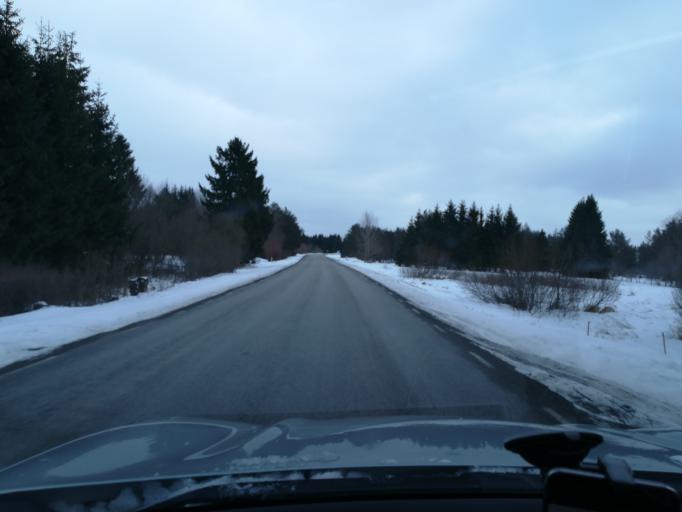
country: EE
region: Harju
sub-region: Keila linn
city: Keila
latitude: 59.3766
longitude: 24.4621
